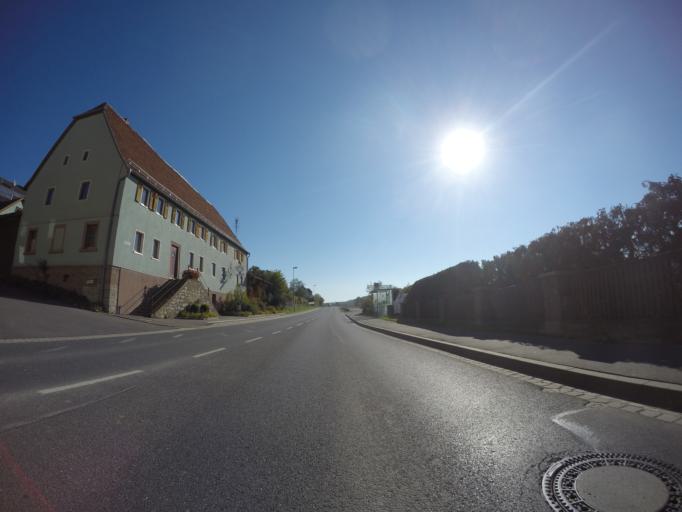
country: DE
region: Bavaria
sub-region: Regierungsbezirk Unterfranken
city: Greussenheim
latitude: 49.7982
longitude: 9.7583
